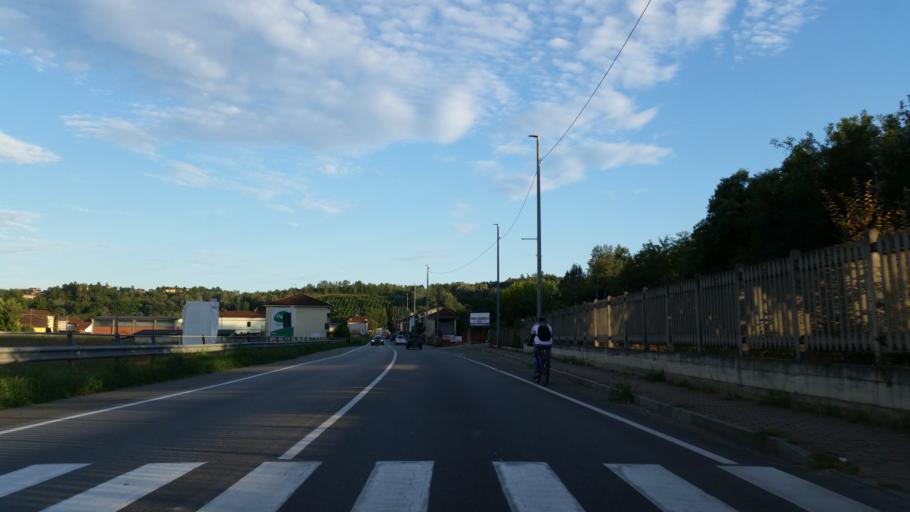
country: IT
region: Piedmont
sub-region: Provincia di Asti
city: Asti
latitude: 44.8828
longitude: 8.2127
